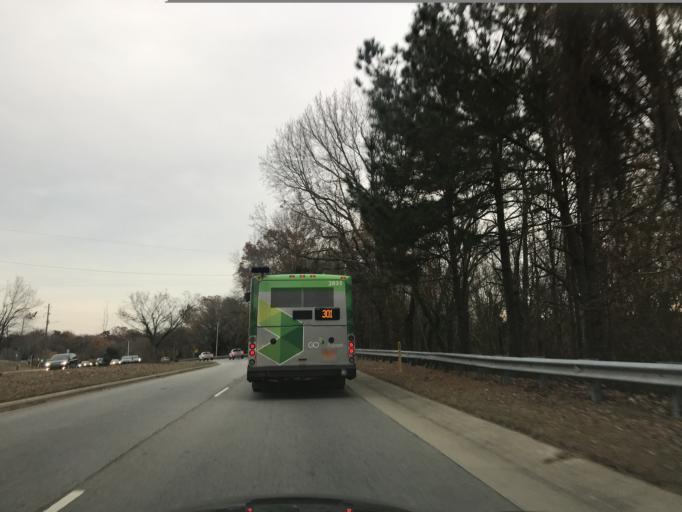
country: US
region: North Carolina
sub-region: Wake County
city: West Raleigh
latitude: 35.7759
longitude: -78.6599
